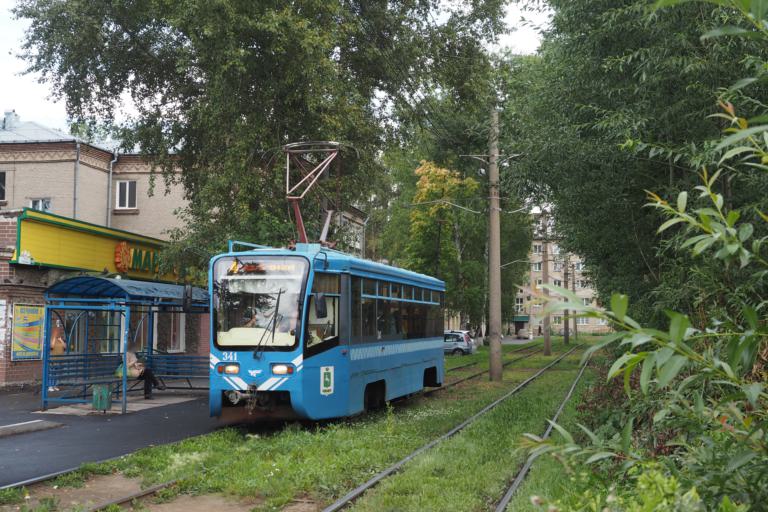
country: RU
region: Tomsk
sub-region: Tomskiy Rayon
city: Tomsk
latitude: 56.4790
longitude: 85.0000
